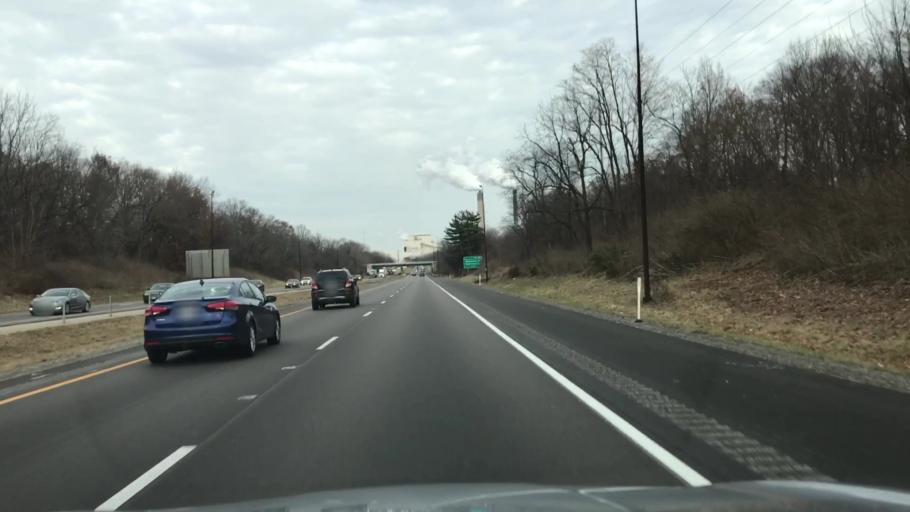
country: US
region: Illinois
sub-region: Sangamon County
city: Southern View
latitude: 39.7472
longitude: -89.6211
